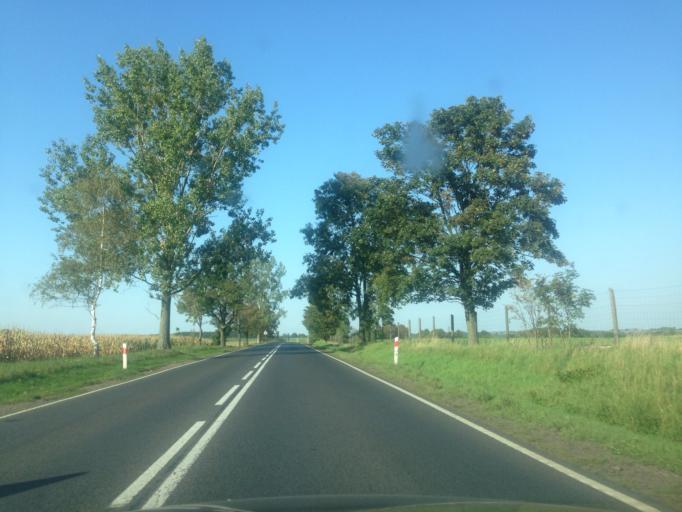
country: PL
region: Kujawsko-Pomorskie
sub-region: Powiat brodnicki
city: Brzozie
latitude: 53.3021
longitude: 19.5056
